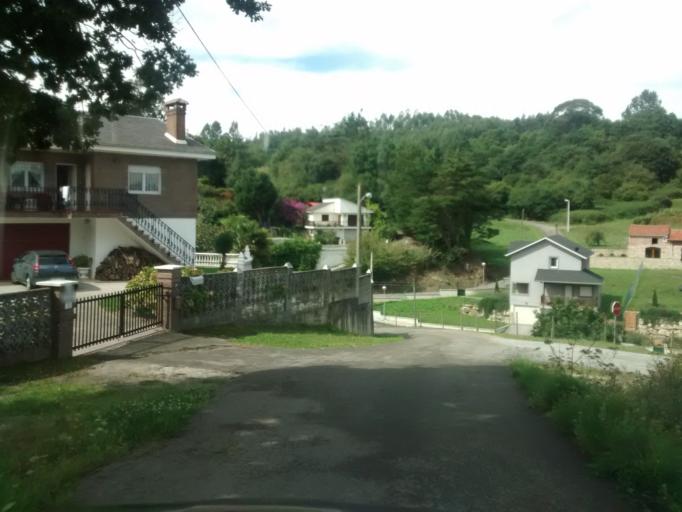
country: ES
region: Cantabria
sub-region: Provincia de Cantabria
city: Miengo
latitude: 43.4094
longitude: -3.9611
